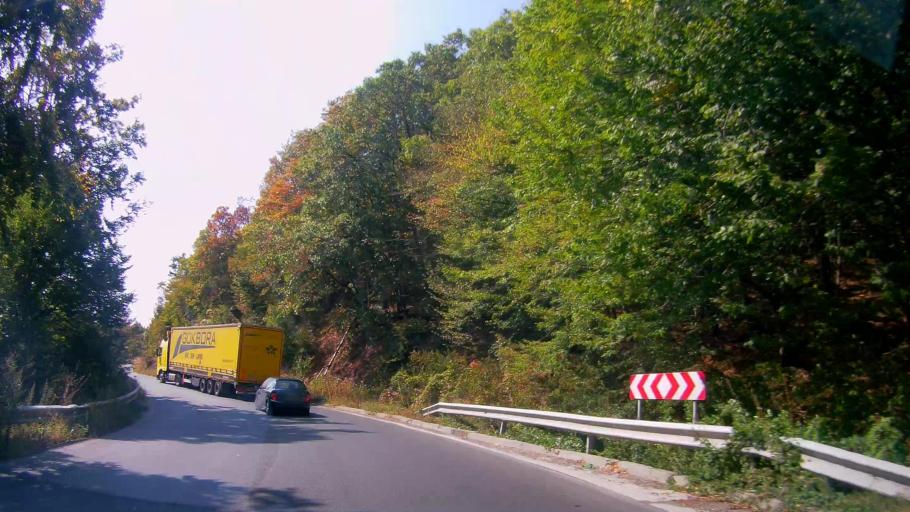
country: BG
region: Shumen
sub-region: Obshtina Smyadovo
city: Smyadovo
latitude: 42.9315
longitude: 26.9485
